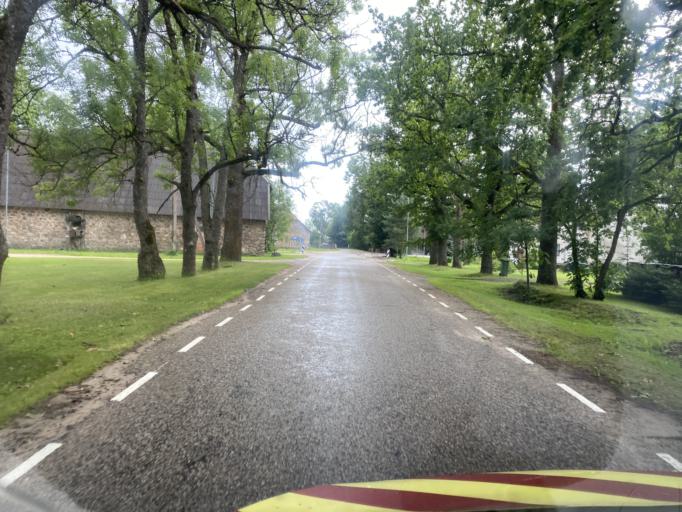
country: EE
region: Valgamaa
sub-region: Torva linn
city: Torva
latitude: 58.0964
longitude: 25.8945
